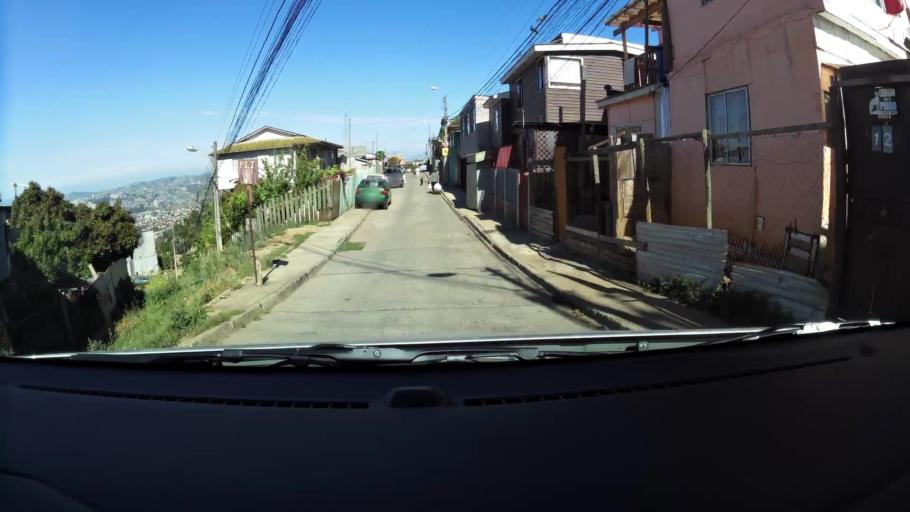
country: CL
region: Valparaiso
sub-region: Provincia de Valparaiso
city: Vina del Mar
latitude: -33.0462
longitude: -71.5599
